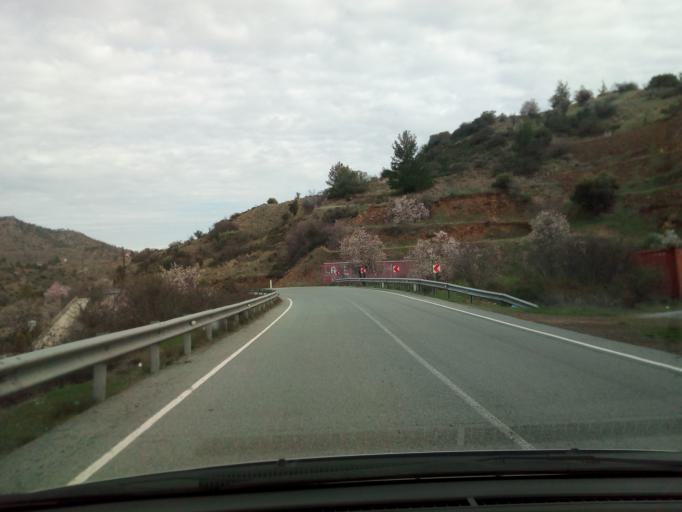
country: CY
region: Lefkosia
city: Klirou
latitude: 34.9679
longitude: 33.1502
